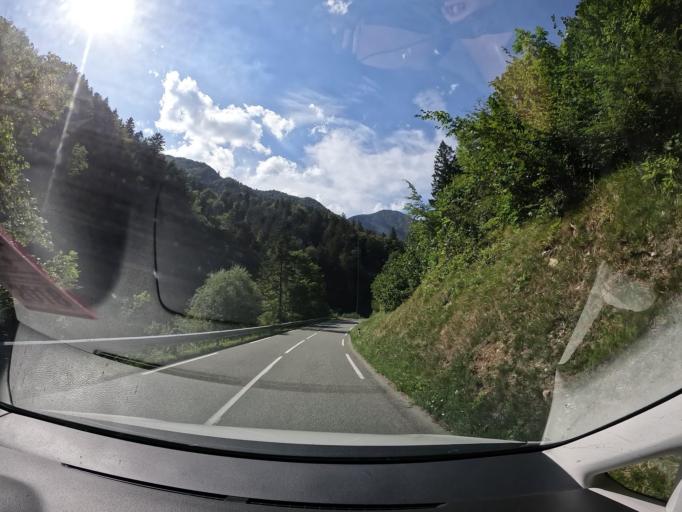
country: SI
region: Jezersko
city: Zgornje Jezersko
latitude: 46.3657
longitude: 14.4473
